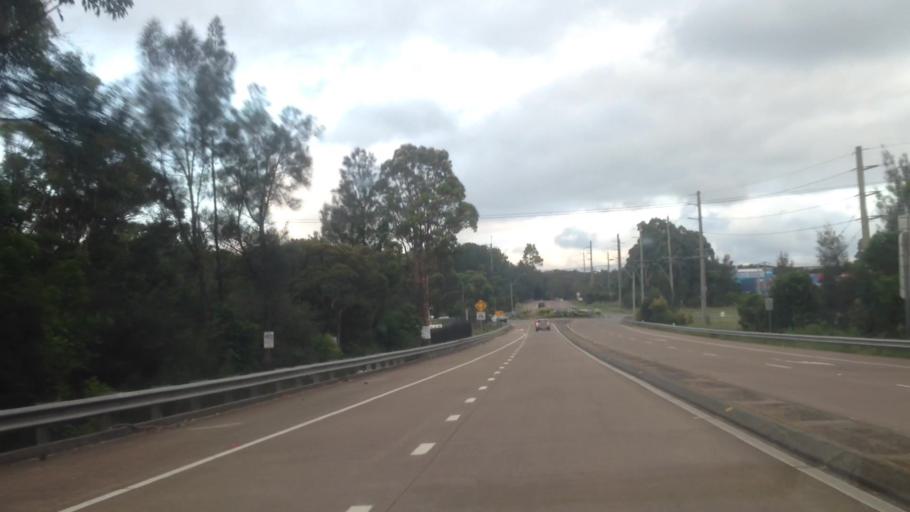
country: AU
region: New South Wales
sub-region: Lake Macquarie Shire
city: Cooranbong
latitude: -33.1170
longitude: 151.4684
